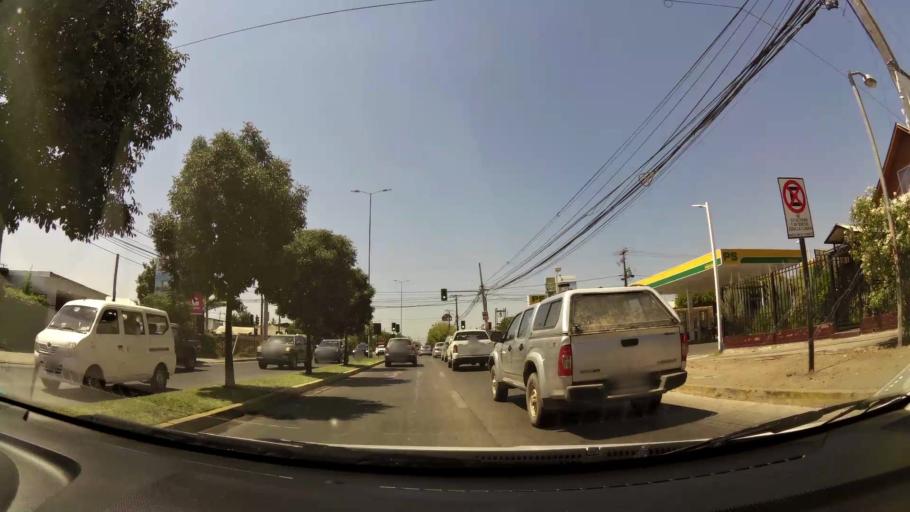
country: CL
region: Maule
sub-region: Provincia de Talca
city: Talca
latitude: -35.4298
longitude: -71.6336
